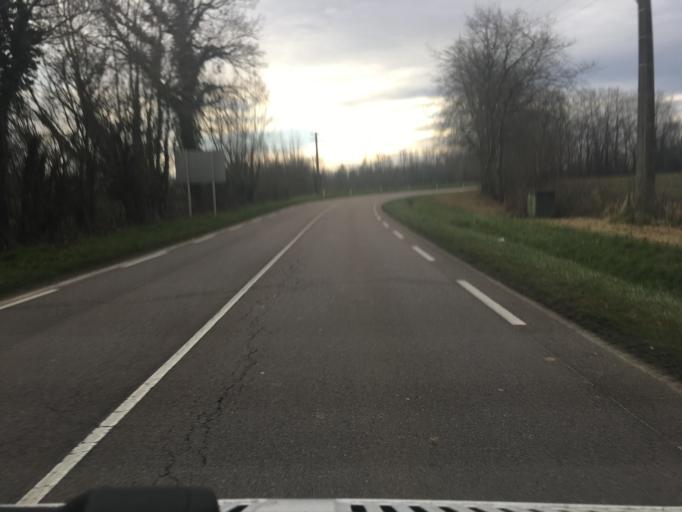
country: FR
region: Haute-Normandie
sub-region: Departement de l'Eure
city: Beuzeville
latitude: 49.3467
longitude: 0.3623
